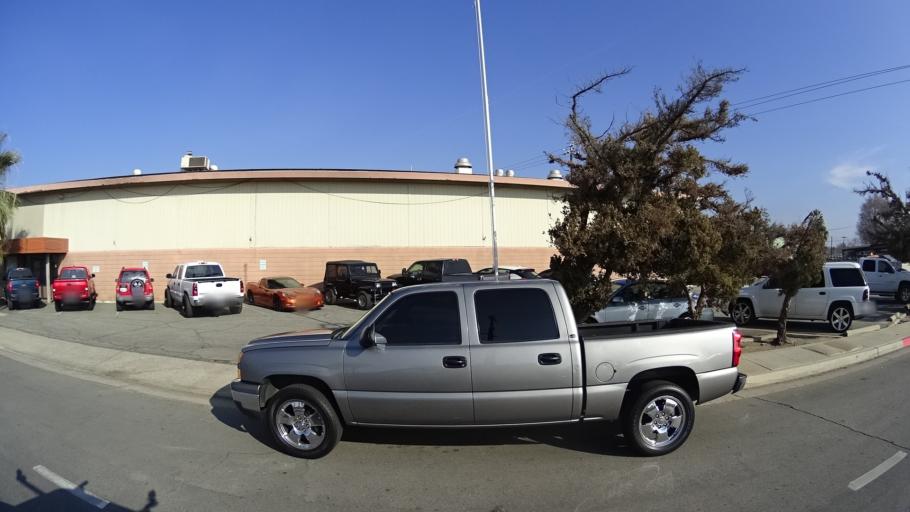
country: US
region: California
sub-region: Kern County
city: Bakersfield
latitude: 35.3867
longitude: -119.0146
